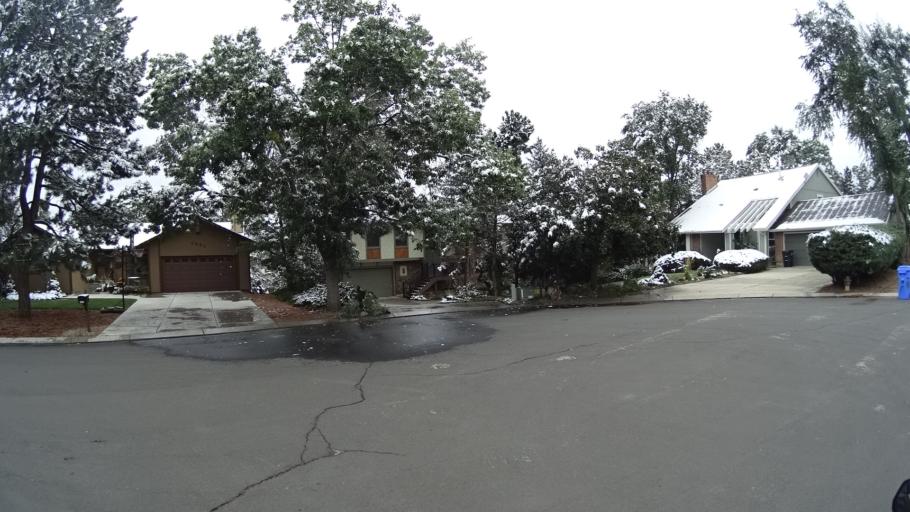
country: US
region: Colorado
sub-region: El Paso County
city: Colorado Springs
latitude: 38.9178
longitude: -104.7895
